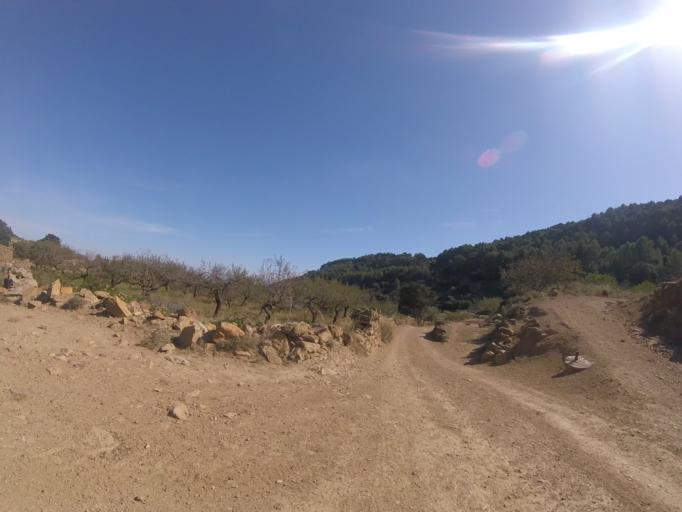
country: ES
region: Valencia
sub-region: Provincia de Castello
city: Sierra-Engarceran
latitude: 40.2735
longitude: -0.0052
